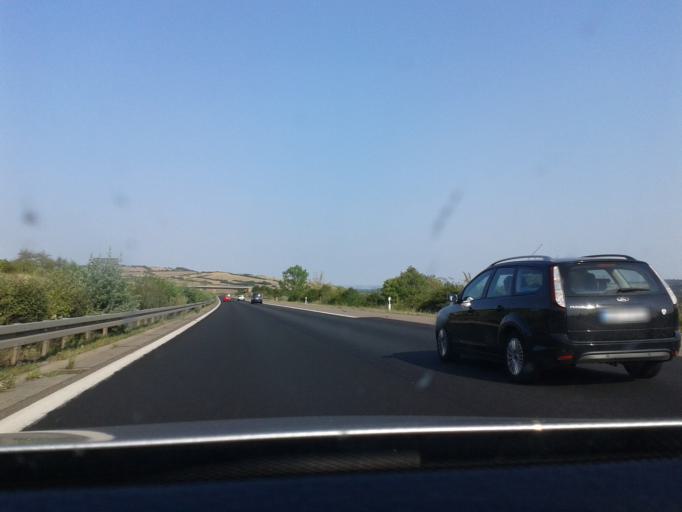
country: DE
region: Saxony-Anhalt
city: Bennungen
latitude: 51.4689
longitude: 11.1057
